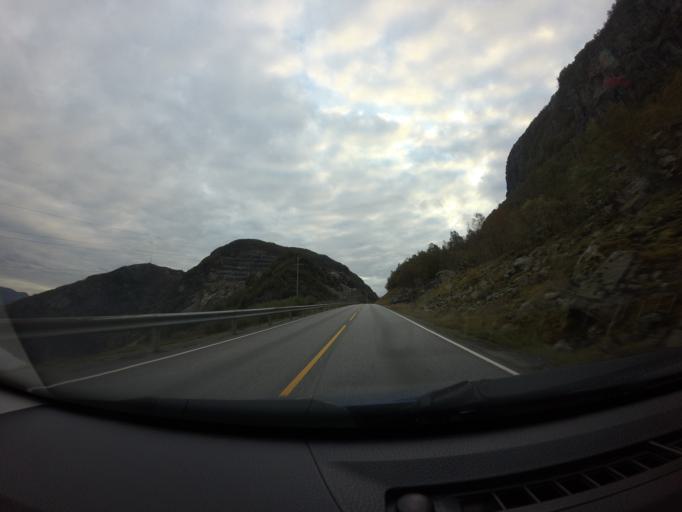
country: NO
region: Rogaland
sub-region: Forsand
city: Forsand
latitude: 58.8370
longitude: 6.1263
